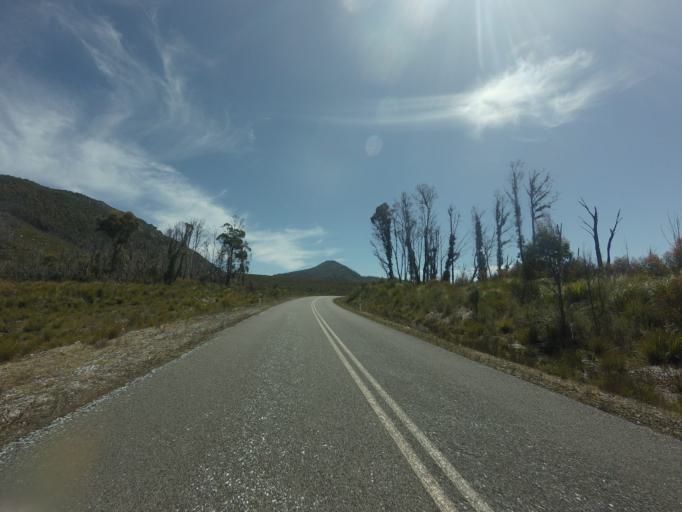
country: AU
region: Tasmania
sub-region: Huon Valley
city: Geeveston
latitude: -42.8589
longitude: 146.1934
